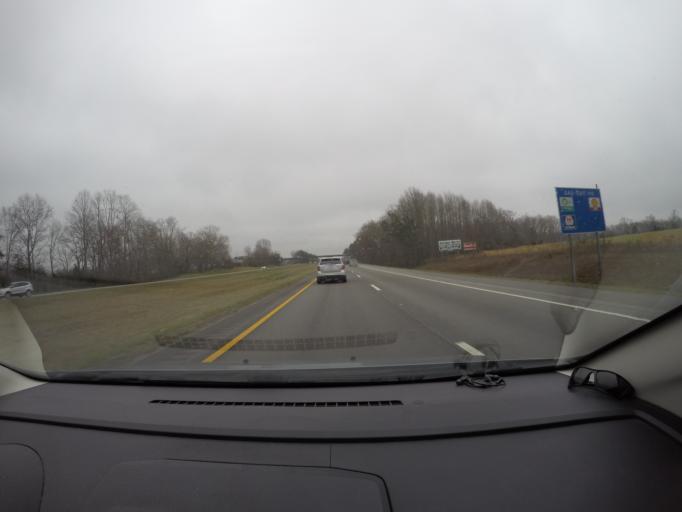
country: US
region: Tennessee
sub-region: Coffee County
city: Manchester
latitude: 35.5099
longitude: -86.1075
